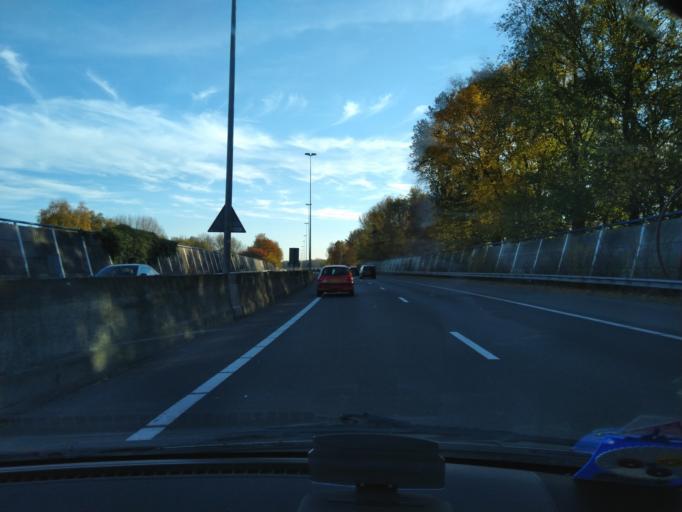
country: NL
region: Groningen
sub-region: Gemeente Groningen
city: Groningen
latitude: 53.1945
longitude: 6.5632
